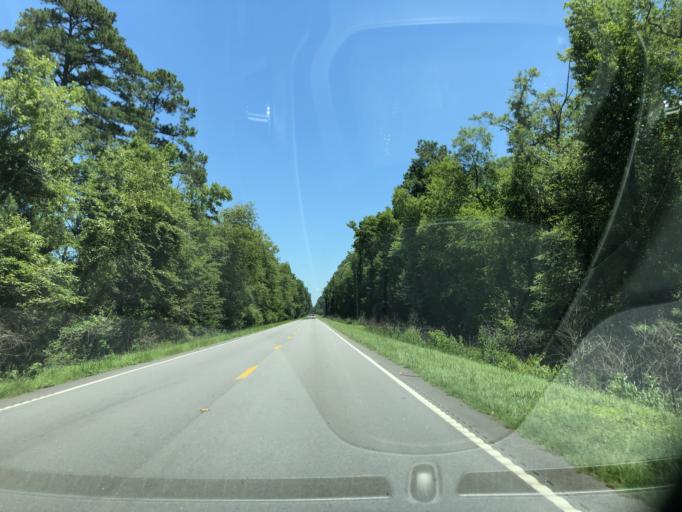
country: US
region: South Carolina
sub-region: Orangeburg County
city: Branchville
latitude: 33.2459
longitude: -80.8422
